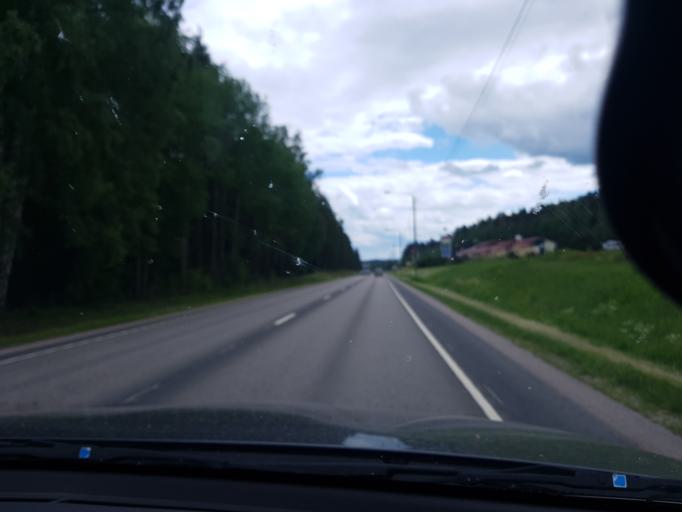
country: FI
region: Pirkanmaa
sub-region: Tampere
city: Paelkaene
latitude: 61.3496
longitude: 24.2549
